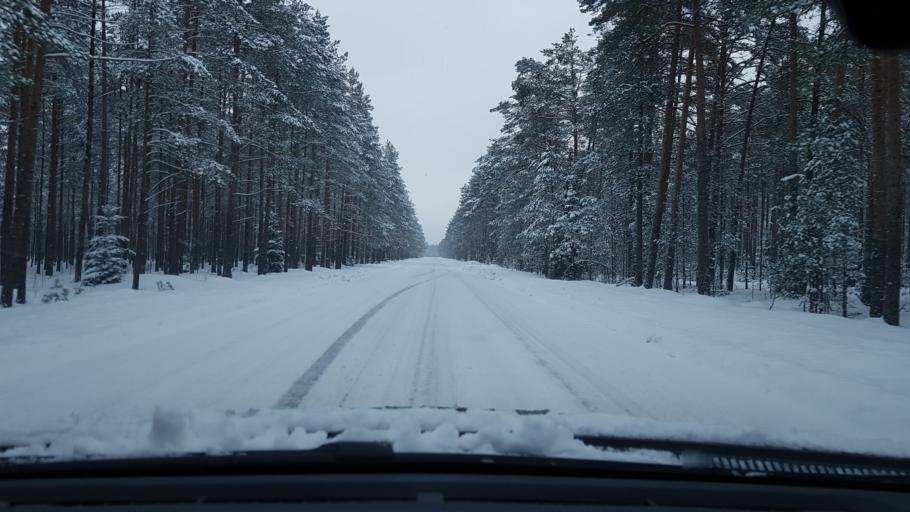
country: EE
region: Harju
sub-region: Kuusalu vald
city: Kuusalu
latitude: 59.4116
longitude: 25.3784
